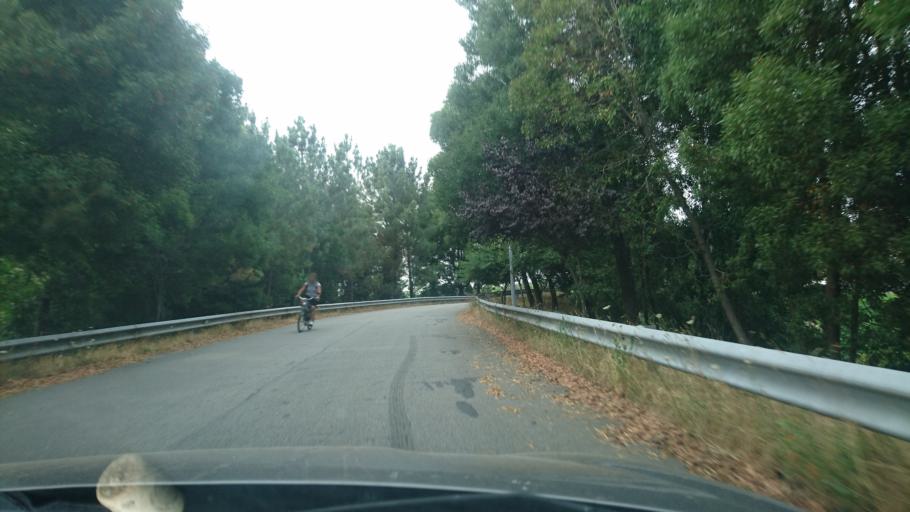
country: PT
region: Porto
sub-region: Paredes
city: Recarei
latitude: 41.1564
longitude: -8.4061
